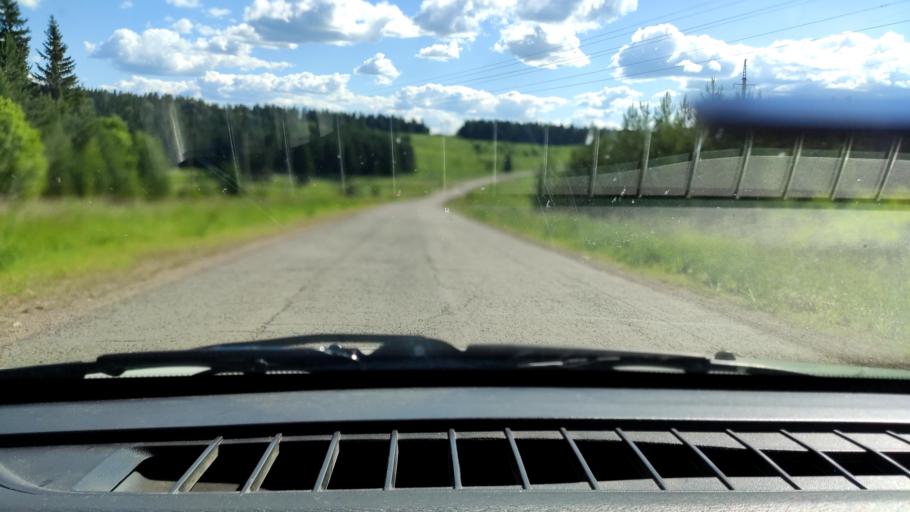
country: RU
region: Perm
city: Uinskoye
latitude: 57.1200
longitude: 56.5518
